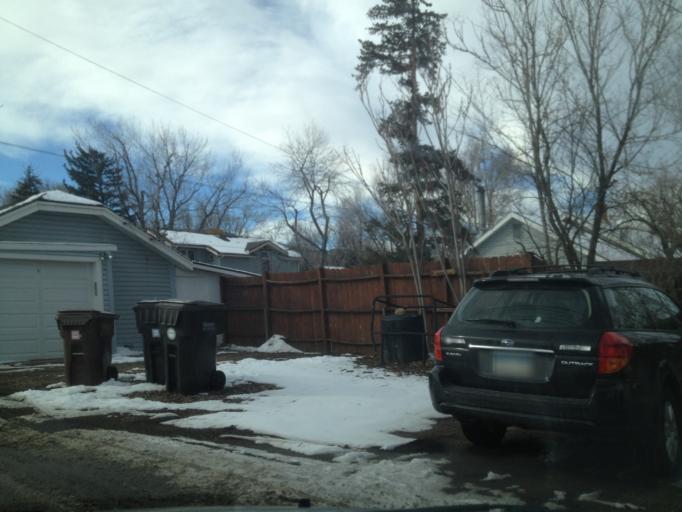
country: US
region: Colorado
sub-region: Boulder County
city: Boulder
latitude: 40.0234
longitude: -105.2610
